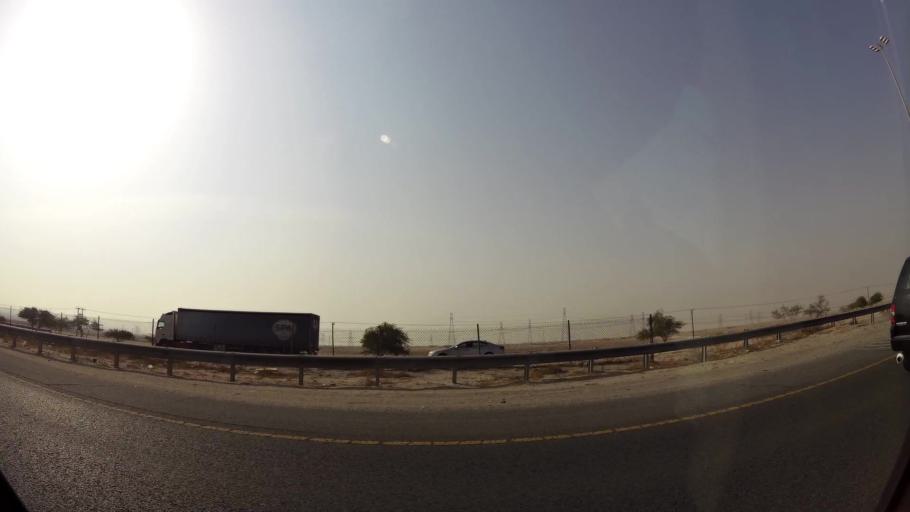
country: KW
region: Al Farwaniyah
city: Janub as Surrah
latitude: 29.1832
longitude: 47.9553
